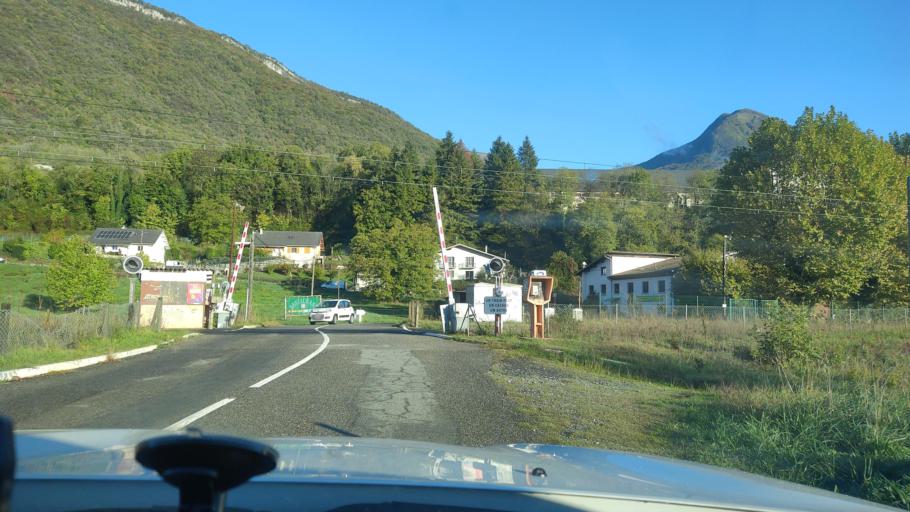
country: FR
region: Rhone-Alpes
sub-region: Departement de la Savoie
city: Cruet
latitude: 45.5169
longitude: 6.0883
